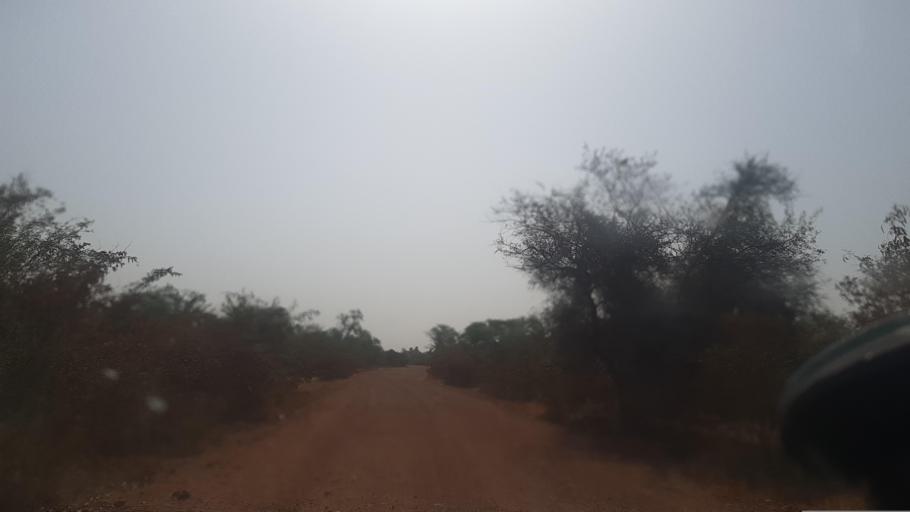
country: ML
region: Segou
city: Baroueli
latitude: 13.0674
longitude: -6.4785
